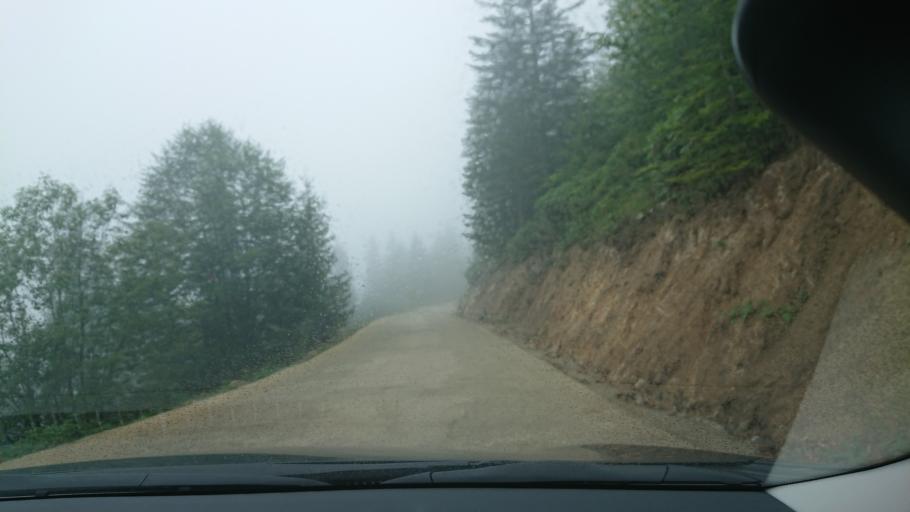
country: TR
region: Gumushane
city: Kurtun
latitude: 40.6624
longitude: 39.0209
